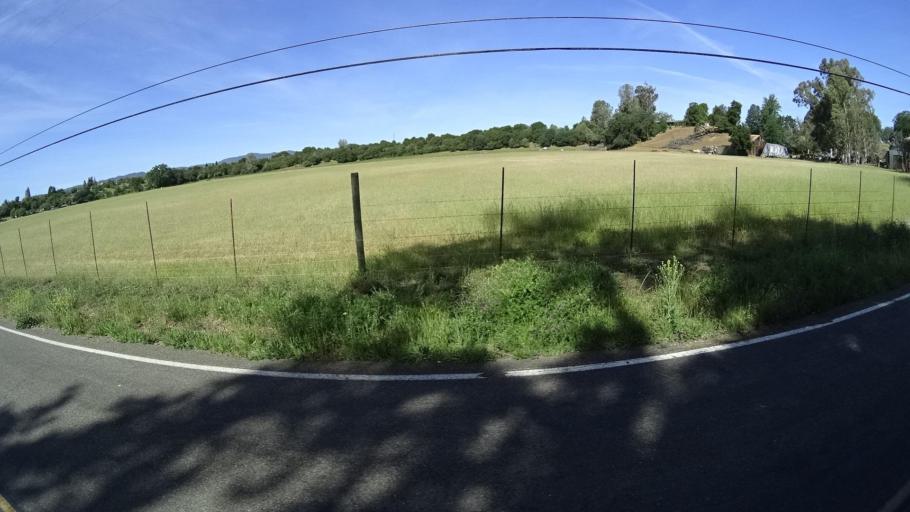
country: US
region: California
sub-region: Lake County
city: Kelseyville
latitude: 38.9685
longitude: -122.8383
